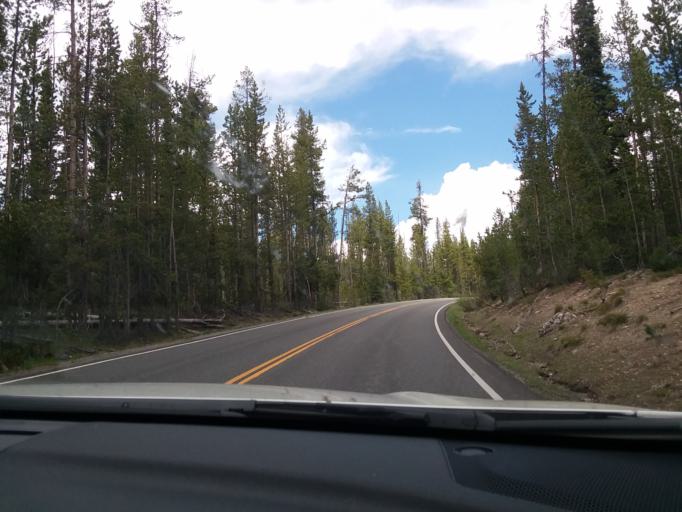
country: US
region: Idaho
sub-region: Teton County
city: Driggs
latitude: 44.1528
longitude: -110.6744
